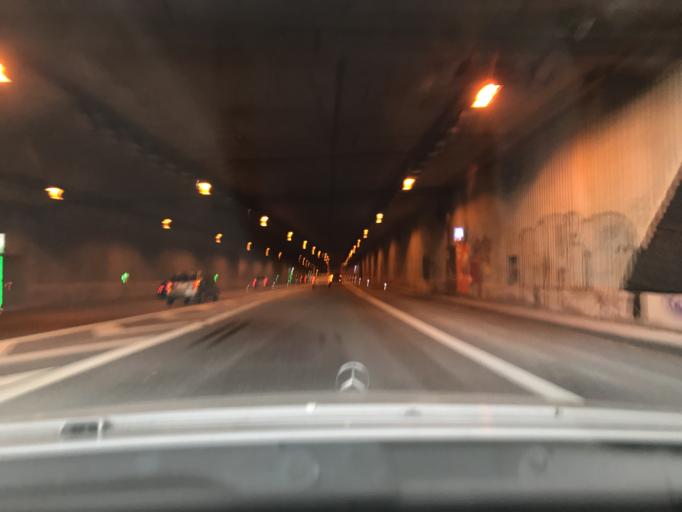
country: DE
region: North Rhine-Westphalia
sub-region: Regierungsbezirk Arnsberg
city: Dortmund
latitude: 51.5088
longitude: 7.5225
